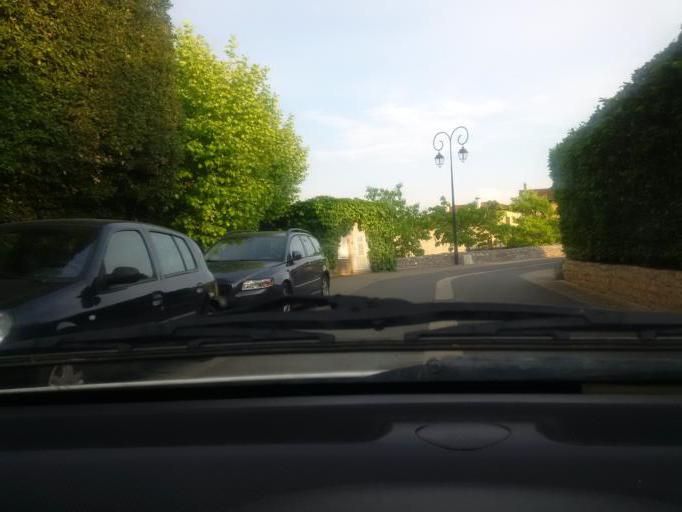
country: FR
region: Rhone-Alpes
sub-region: Departement du Rhone
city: Lucenay
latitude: 45.9114
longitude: 4.7013
